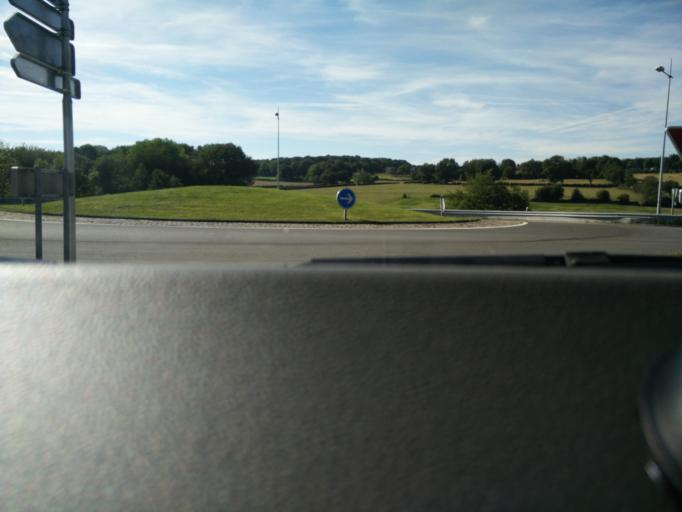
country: FR
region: Nord-Pas-de-Calais
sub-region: Departement du Nord
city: Trelon
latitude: 50.1238
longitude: 4.0806
